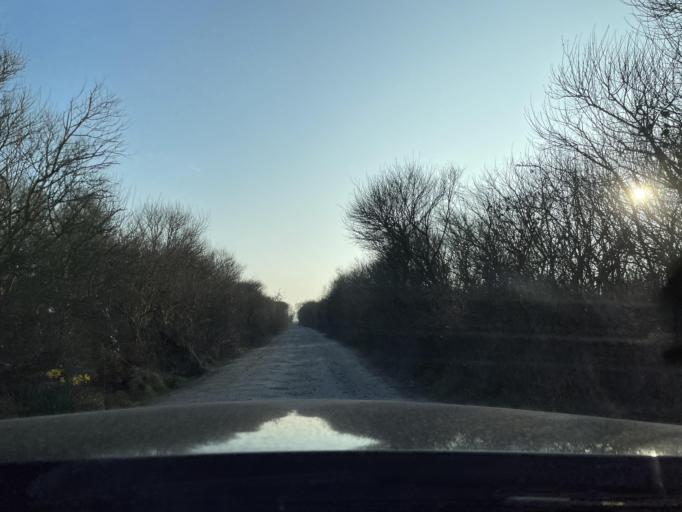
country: GB
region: England
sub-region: Norfolk
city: Martham
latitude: 52.7580
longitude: 1.6491
